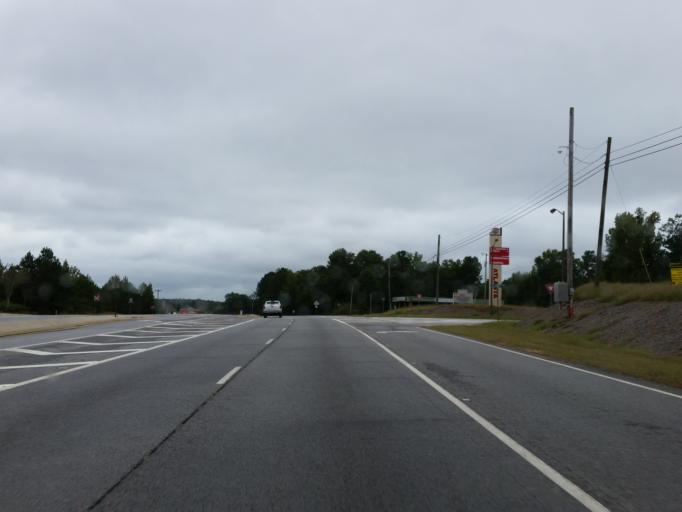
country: US
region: Georgia
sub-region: Henry County
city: Hampton
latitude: 33.3959
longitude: -84.3117
